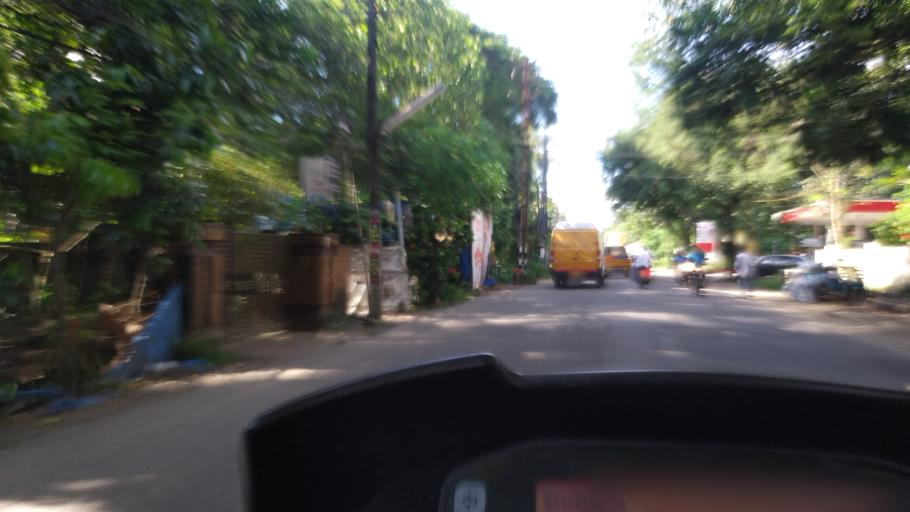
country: IN
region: Kerala
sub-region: Ernakulam
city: Elur
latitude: 10.0311
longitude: 76.2218
